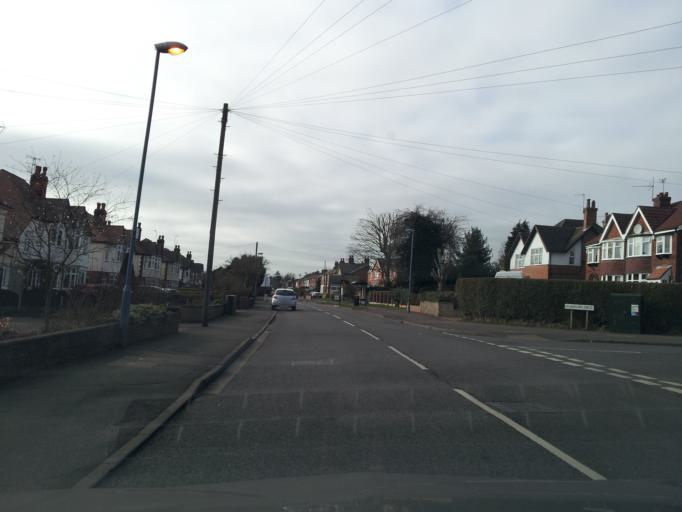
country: GB
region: England
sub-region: Derbyshire
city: Findern
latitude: 52.9100
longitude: -1.5367
